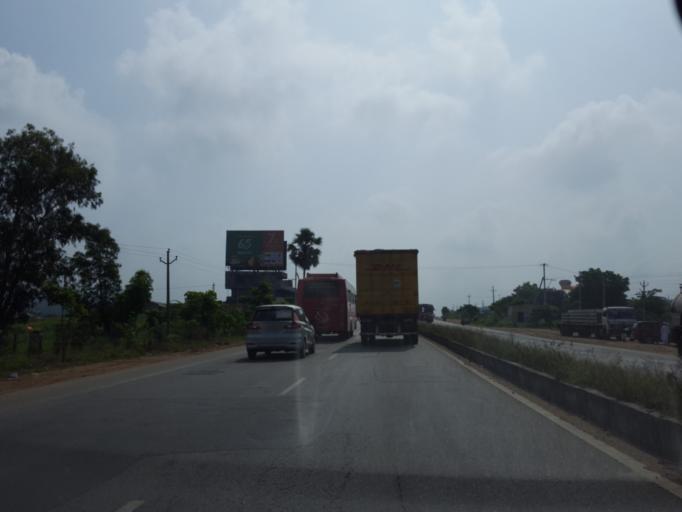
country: IN
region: Telangana
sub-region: Rangareddi
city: Ghatkesar
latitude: 17.2897
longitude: 78.7671
